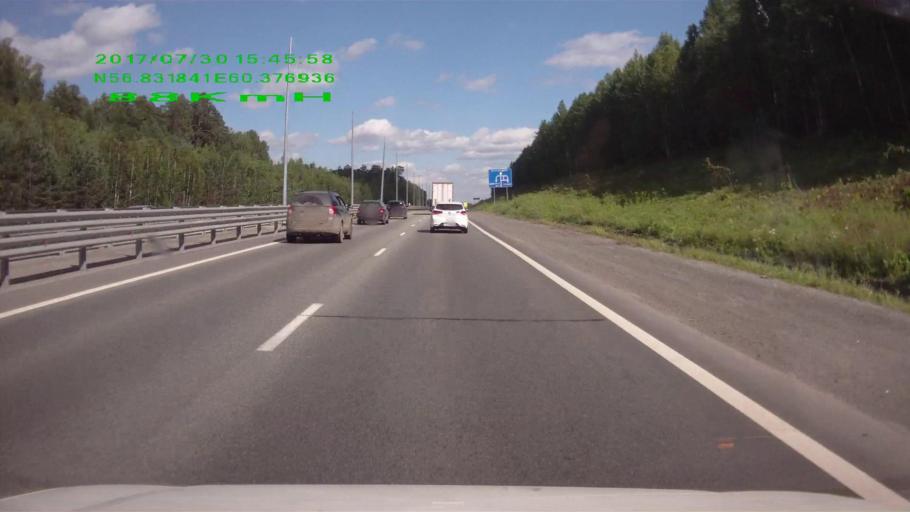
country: RU
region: Sverdlovsk
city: Severka
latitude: 56.8318
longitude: 60.3776
